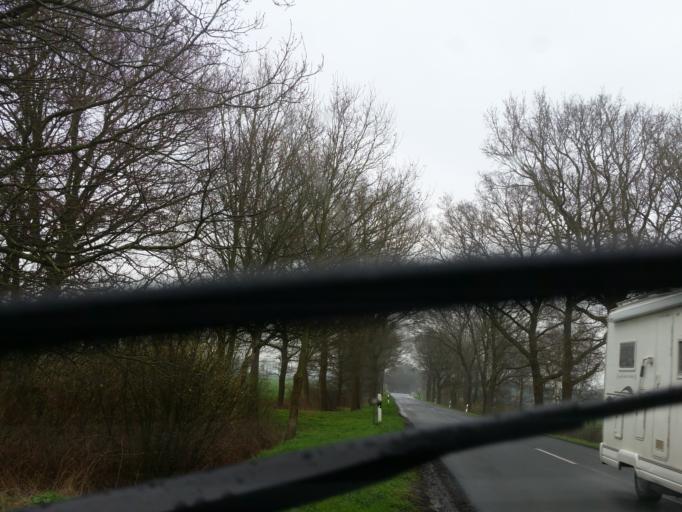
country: DE
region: Lower Saxony
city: Hipstedt
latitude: 53.5588
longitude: 8.9850
